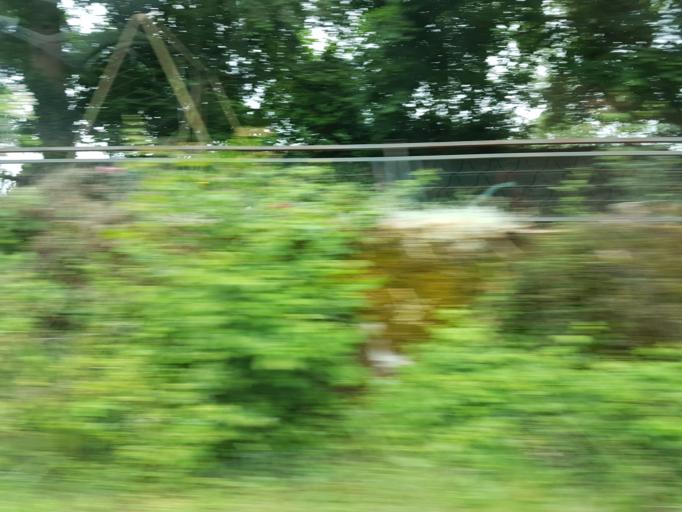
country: FR
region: Bourgogne
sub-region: Departement de la Nievre
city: Lormes
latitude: 47.1655
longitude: 3.8385
